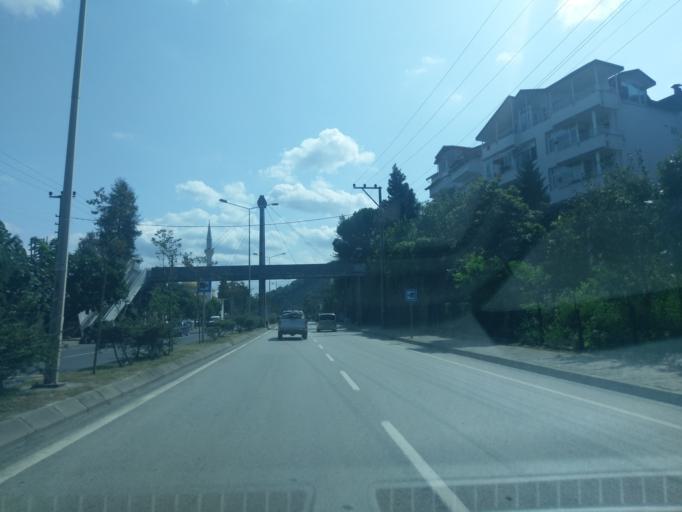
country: TR
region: Ordu
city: Ordu
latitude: 41.0049
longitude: 37.8700
